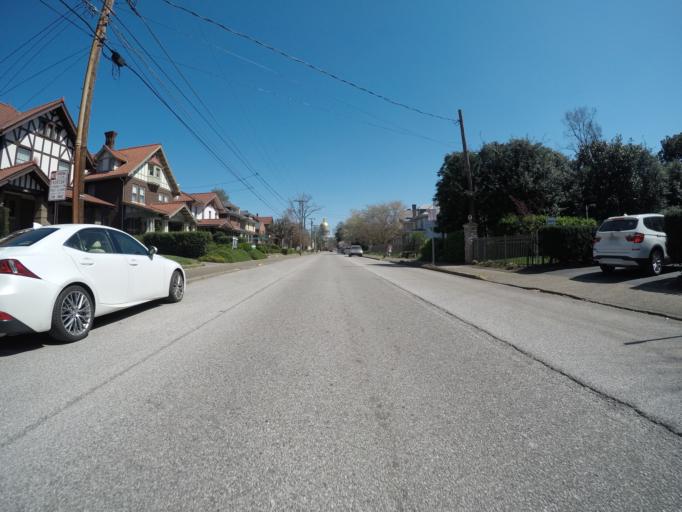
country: US
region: West Virginia
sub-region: Kanawha County
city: Charleston
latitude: 38.3392
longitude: -81.6200
